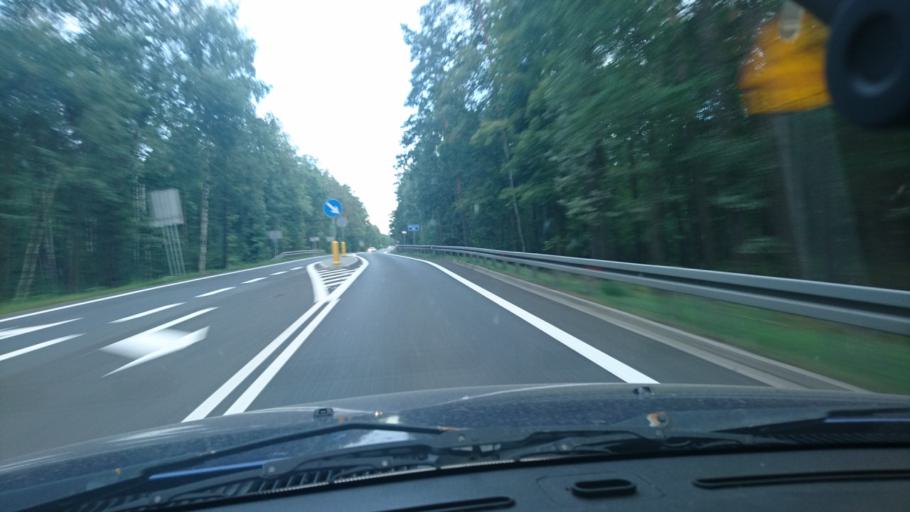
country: PL
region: Silesian Voivodeship
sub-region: Powiat lubliniecki
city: Lubliniec
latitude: 50.6106
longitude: 18.6940
